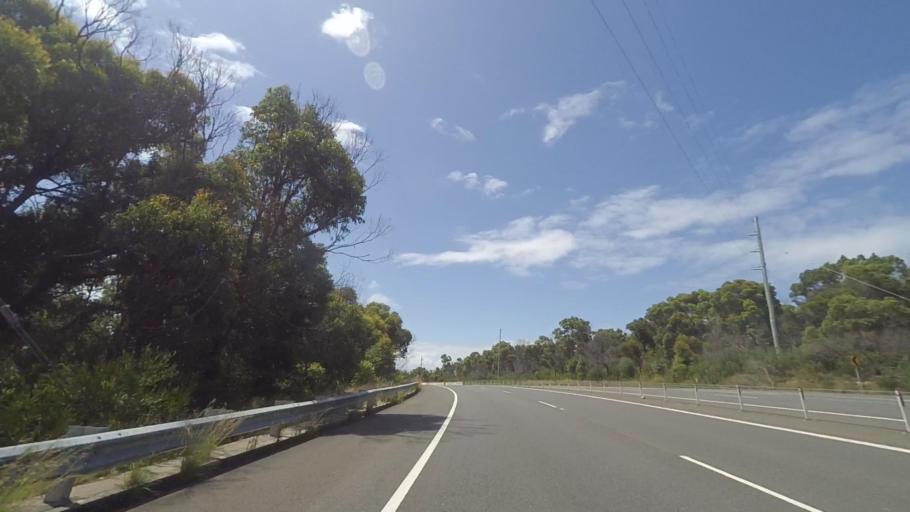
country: AU
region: New South Wales
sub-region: Wyong Shire
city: Kingfisher Shores
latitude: -33.1616
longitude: 151.6125
